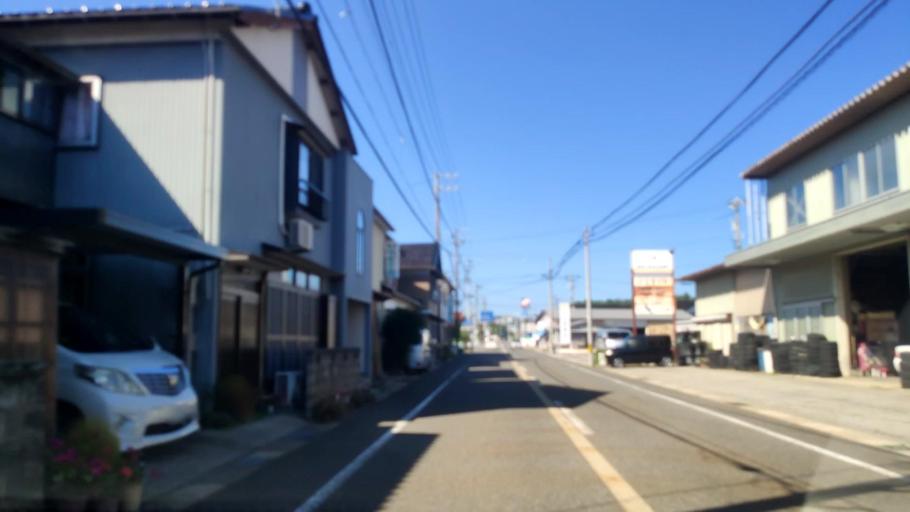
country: JP
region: Ishikawa
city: Nanao
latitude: 37.4422
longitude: 137.2647
